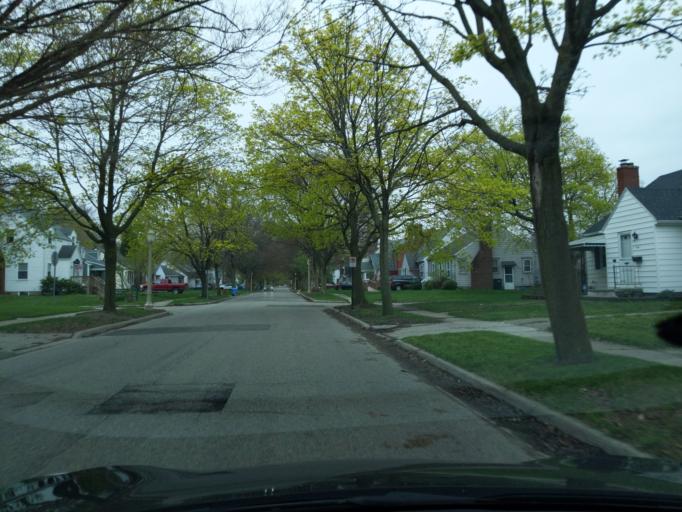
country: US
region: Michigan
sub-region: Ingham County
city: Edgemont Park
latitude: 42.7478
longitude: -84.5766
